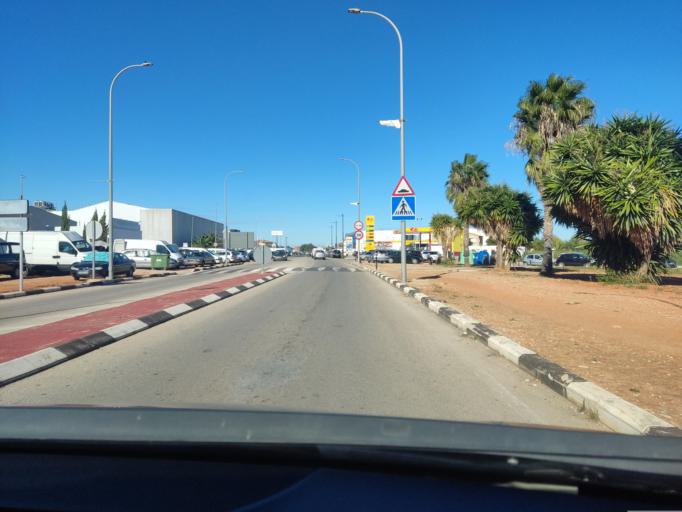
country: ES
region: Valencia
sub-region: Provincia de Alicante
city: Vergel
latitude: 38.8536
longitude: 0.0015
